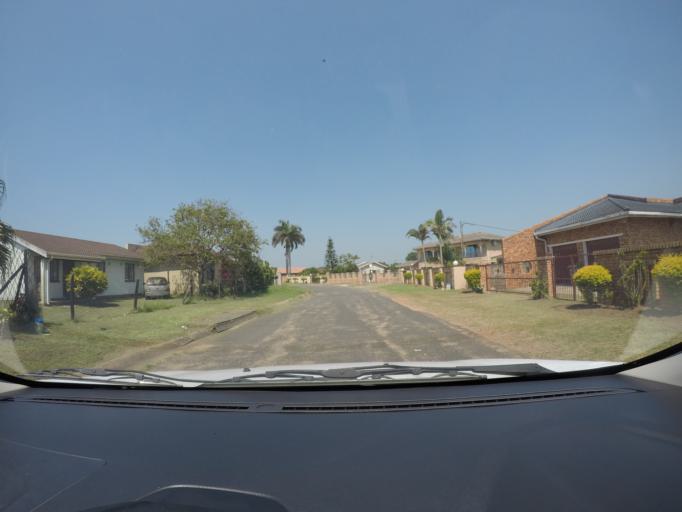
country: ZA
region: KwaZulu-Natal
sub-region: uThungulu District Municipality
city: eSikhawini
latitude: -28.8612
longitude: 31.9233
